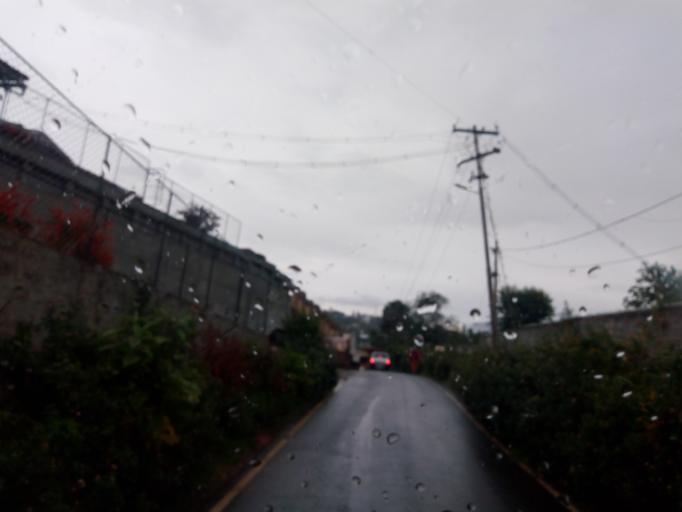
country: IN
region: Tamil Nadu
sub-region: Nilgiri
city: Wellington
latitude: 11.3508
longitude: 76.8095
